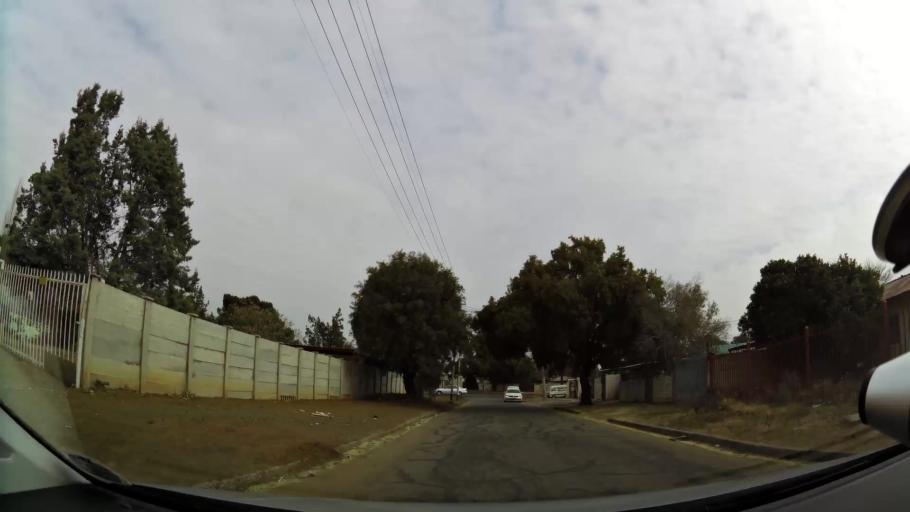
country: ZA
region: Orange Free State
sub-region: Mangaung Metropolitan Municipality
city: Bloemfontein
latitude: -29.1270
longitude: 26.1912
